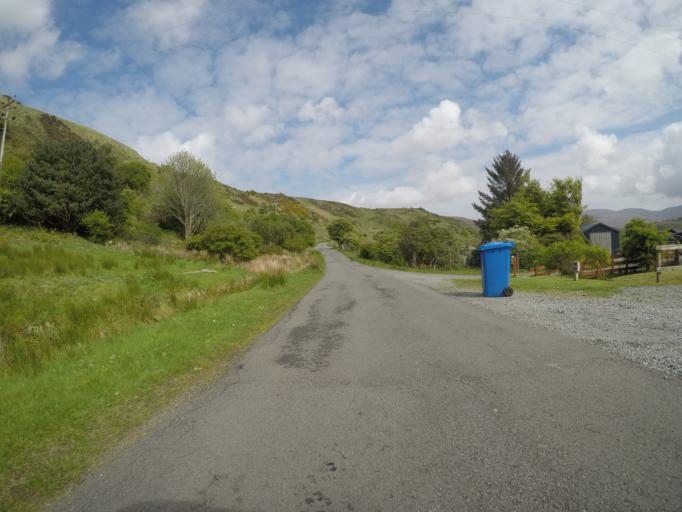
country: GB
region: Scotland
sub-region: Highland
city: Portree
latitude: 57.5914
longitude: -6.3754
